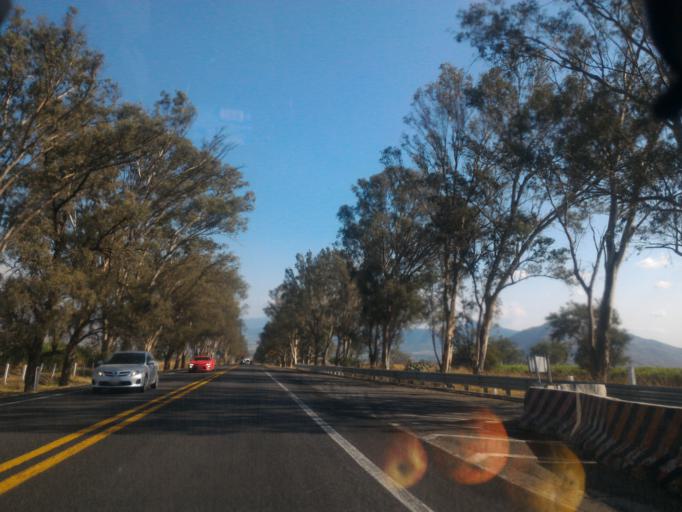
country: MX
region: Jalisco
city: Tuxpan
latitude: 19.5545
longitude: -103.4378
